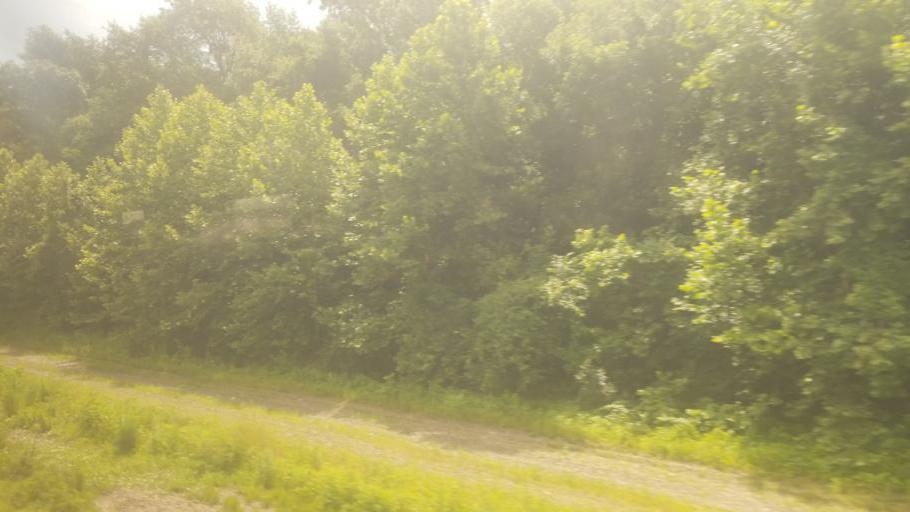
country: US
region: Missouri
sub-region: Jackson County
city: East Independence
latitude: 39.1568
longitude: -94.3703
